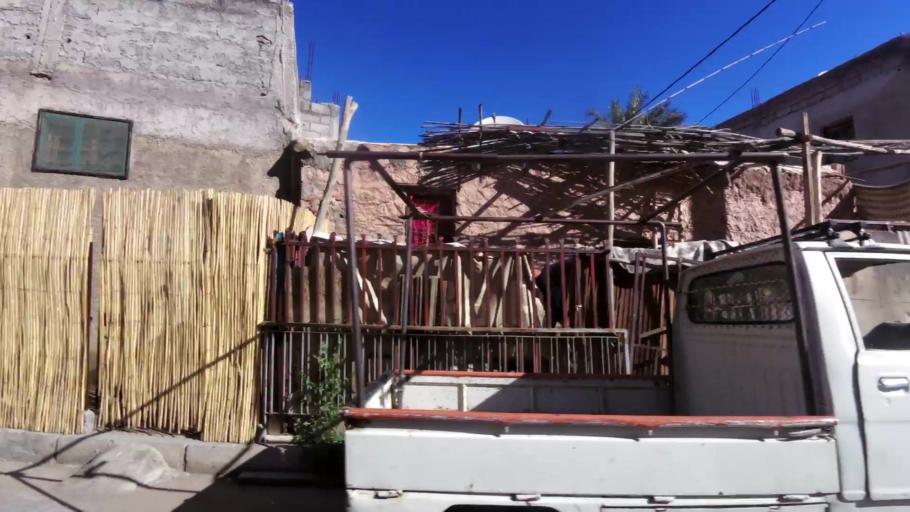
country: MA
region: Marrakech-Tensift-Al Haouz
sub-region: Marrakech
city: Marrakesh
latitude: 31.6012
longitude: -8.0332
